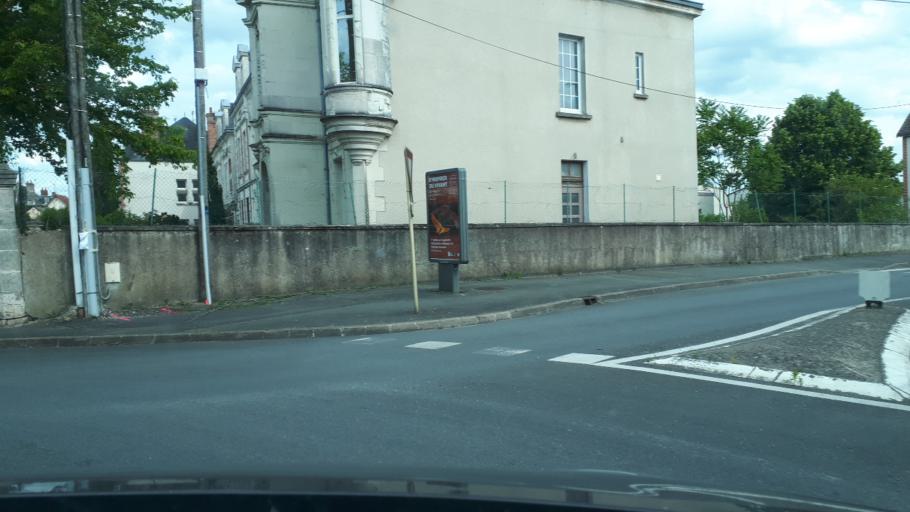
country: FR
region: Centre
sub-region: Departement du Loir-et-Cher
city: Romorantin-Lanthenay
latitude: 47.3553
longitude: 1.7397
